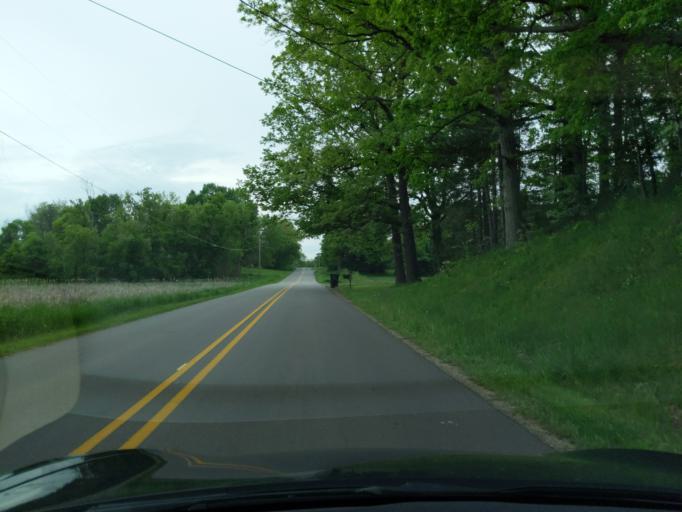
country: US
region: Michigan
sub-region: Jackson County
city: Jackson
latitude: 42.3490
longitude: -84.3486
